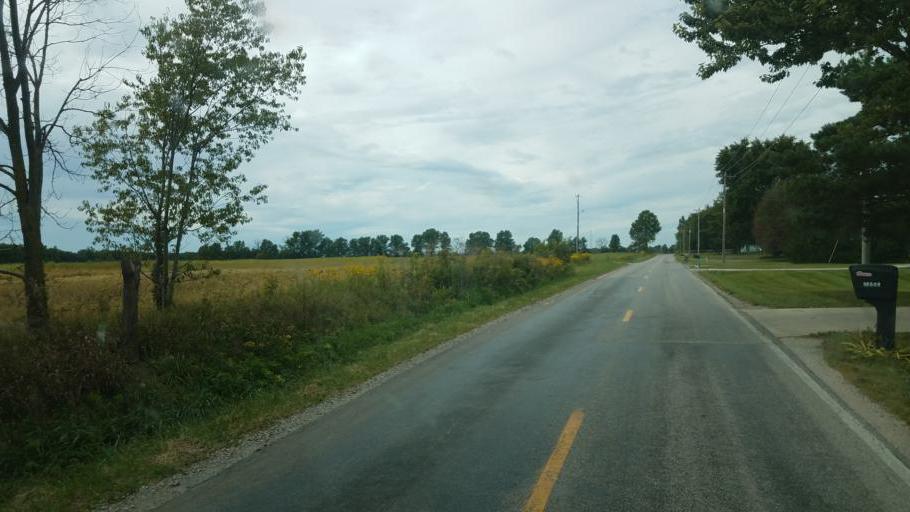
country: US
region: Ohio
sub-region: Knox County
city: Centerburg
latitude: 40.2614
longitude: -82.7606
